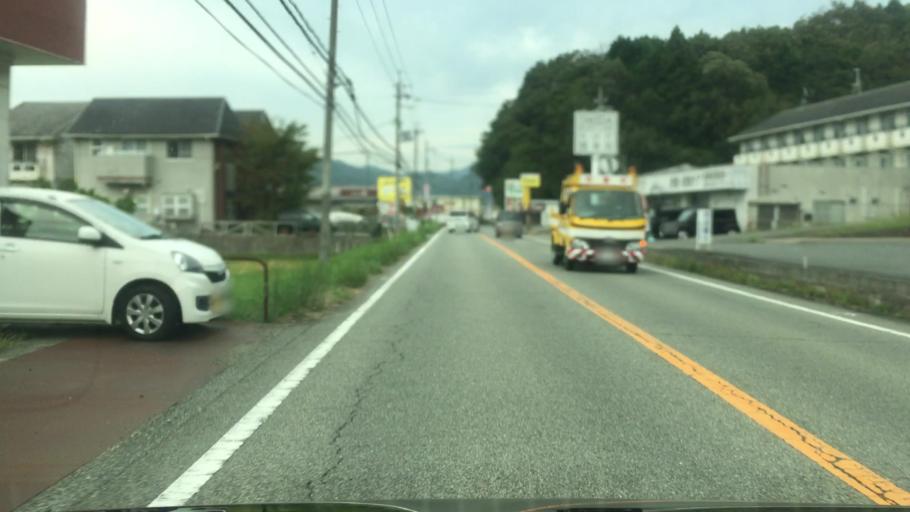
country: JP
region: Hyogo
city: Sasayama
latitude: 35.0666
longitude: 135.1940
